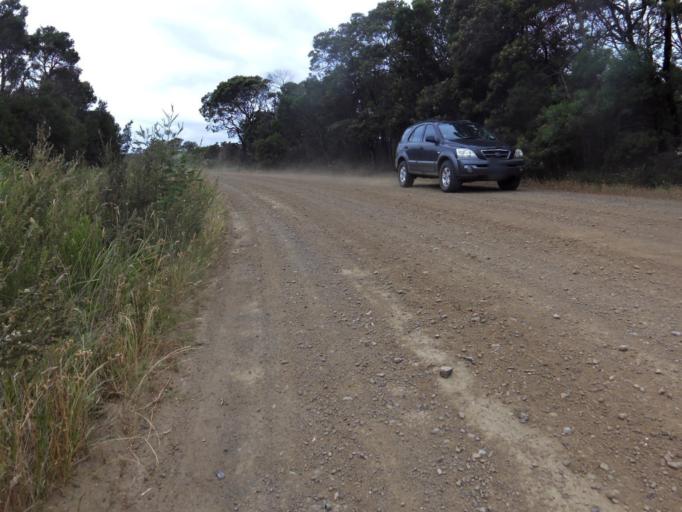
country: AU
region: Victoria
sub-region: Bass Coast
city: Cowes
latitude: -38.3822
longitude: 145.2834
